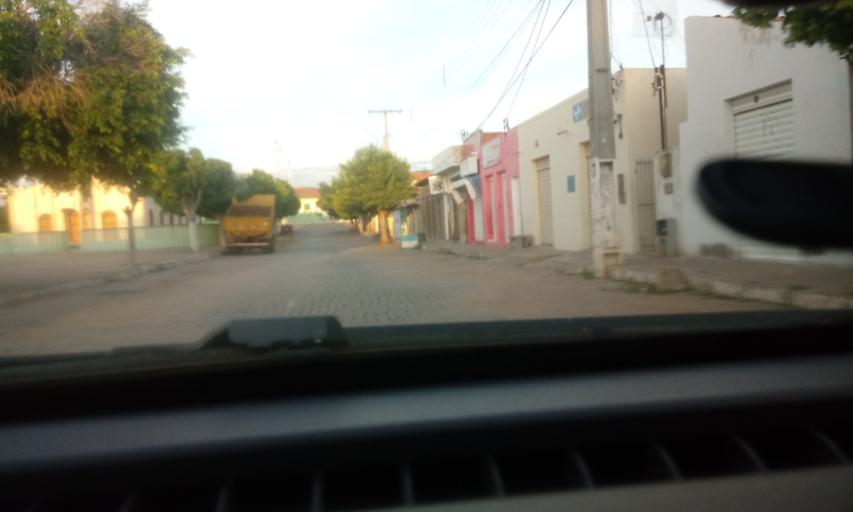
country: BR
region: Bahia
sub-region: Riacho De Santana
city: Riacho de Santana
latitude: -13.9111
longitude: -42.8460
